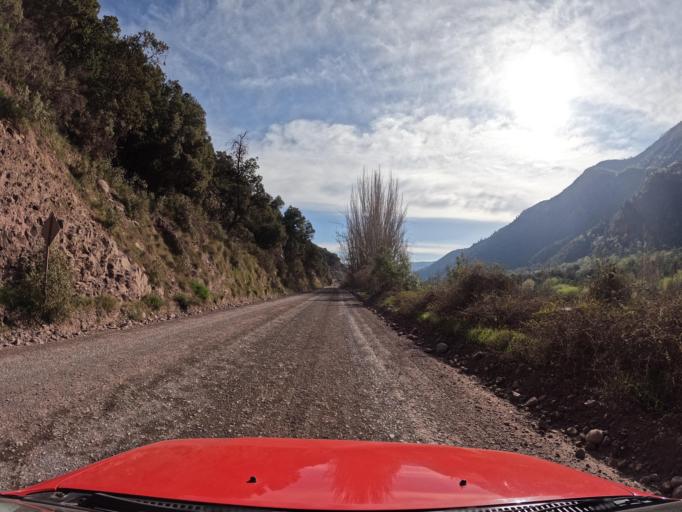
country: CL
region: O'Higgins
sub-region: Provincia de Colchagua
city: Chimbarongo
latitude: -35.0002
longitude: -70.7865
